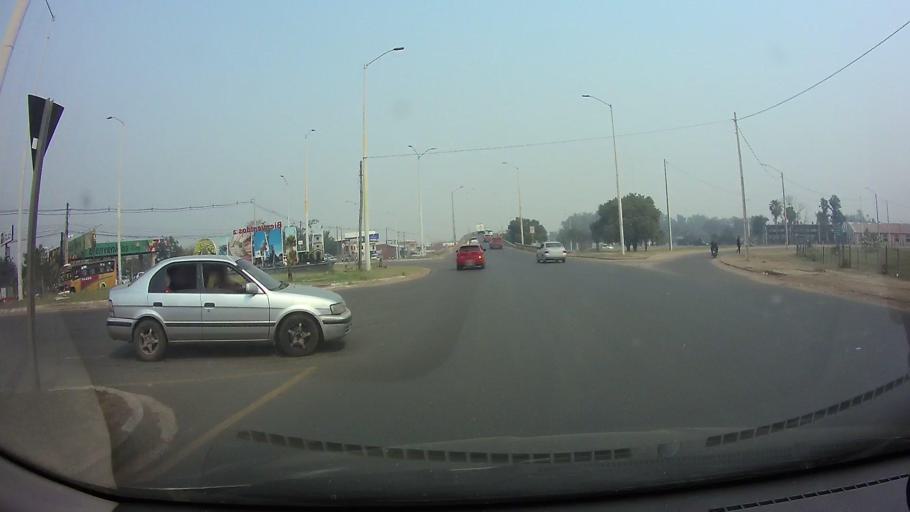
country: PY
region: Central
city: Limpio
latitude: -25.1757
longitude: -57.4848
